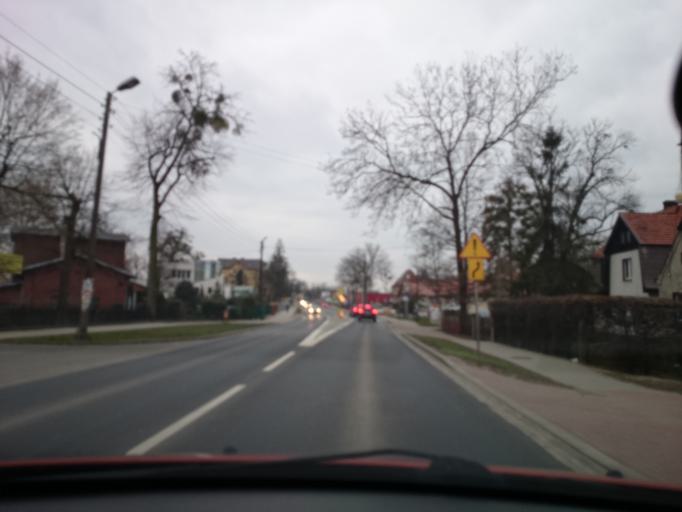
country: PL
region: Opole Voivodeship
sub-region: Powiat opolski
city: Niemodlin
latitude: 50.6421
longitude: 17.6325
